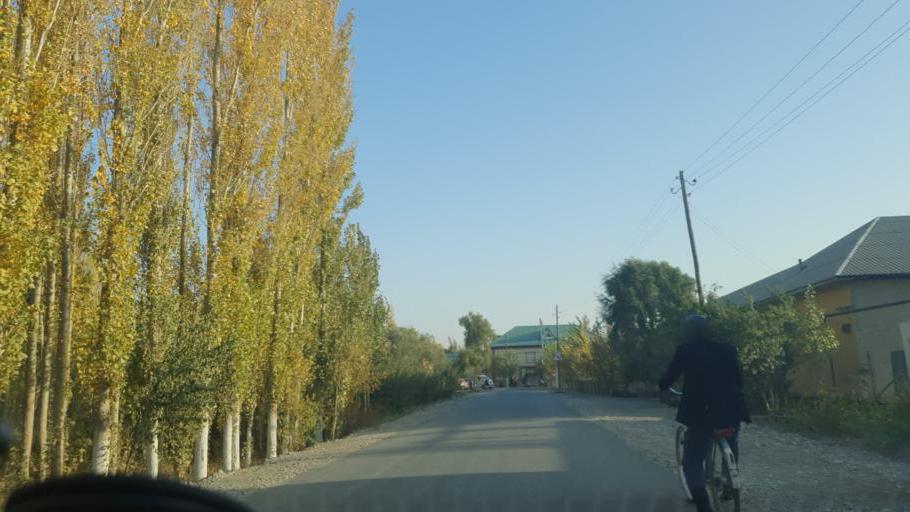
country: UZ
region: Fergana
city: Beshariq
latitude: 40.4629
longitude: 70.5435
